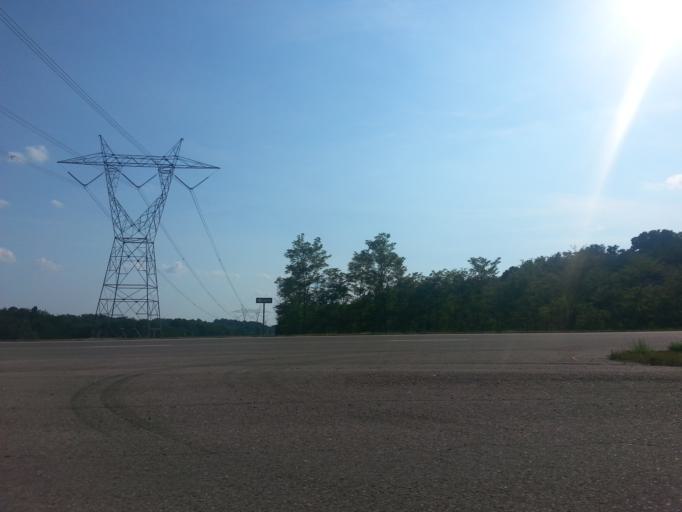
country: US
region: Tennessee
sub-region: Loudon County
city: Lenoir City
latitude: 35.7443
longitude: -84.2126
